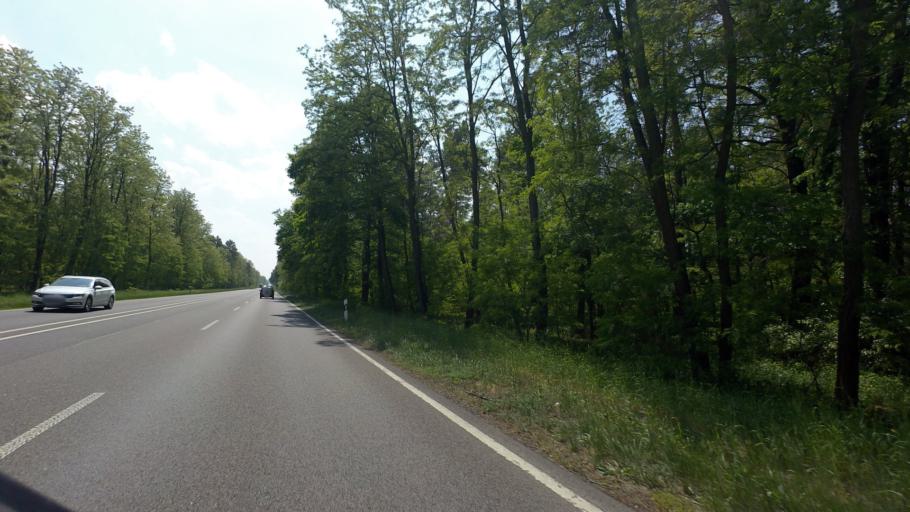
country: DE
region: Brandenburg
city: Spremberg
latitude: 51.6489
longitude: 14.3614
